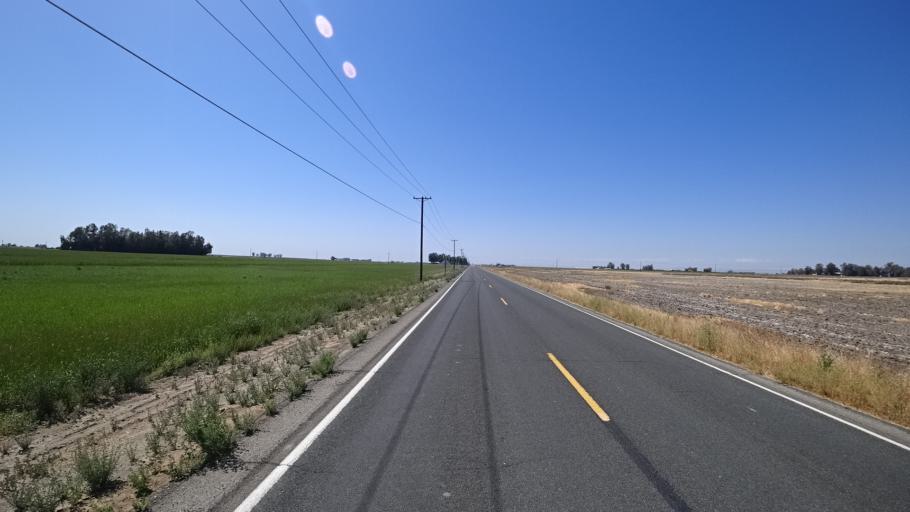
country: US
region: California
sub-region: Kings County
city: Stratford
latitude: 36.2074
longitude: -119.7802
